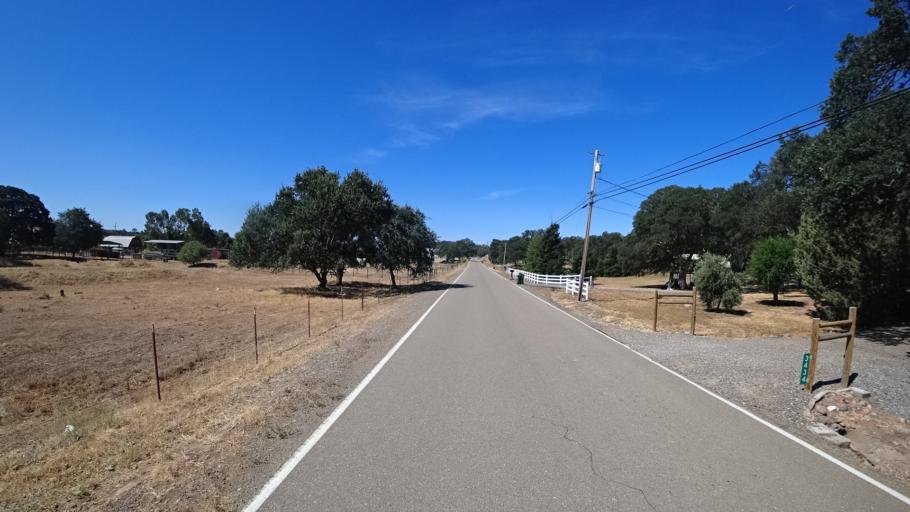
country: US
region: California
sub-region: Calaveras County
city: Rancho Calaveras
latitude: 38.1487
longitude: -120.8612
